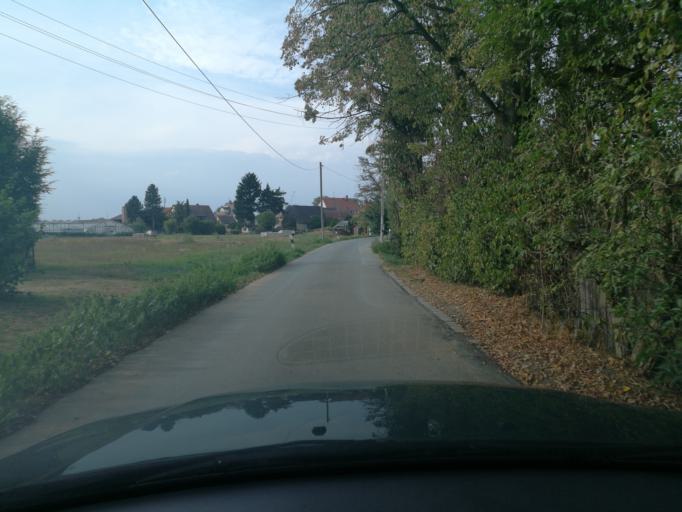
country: DE
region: Bavaria
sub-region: Regierungsbezirk Mittelfranken
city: Wetzendorf
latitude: 49.4880
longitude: 11.0640
